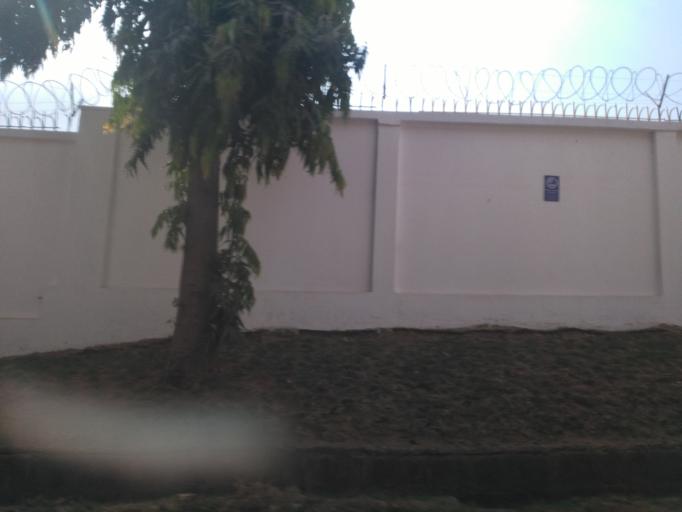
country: TZ
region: Dar es Salaam
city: Dar es Salaam
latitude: -6.7989
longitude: 39.2768
